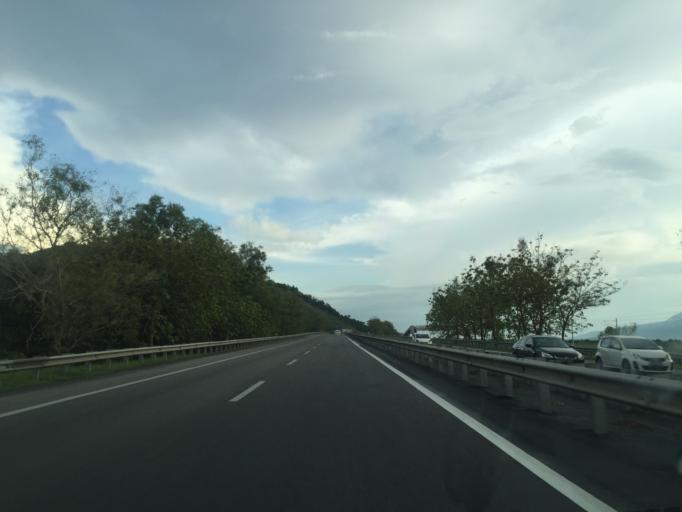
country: MY
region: Kedah
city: Gurun
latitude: 5.9455
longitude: 100.4563
